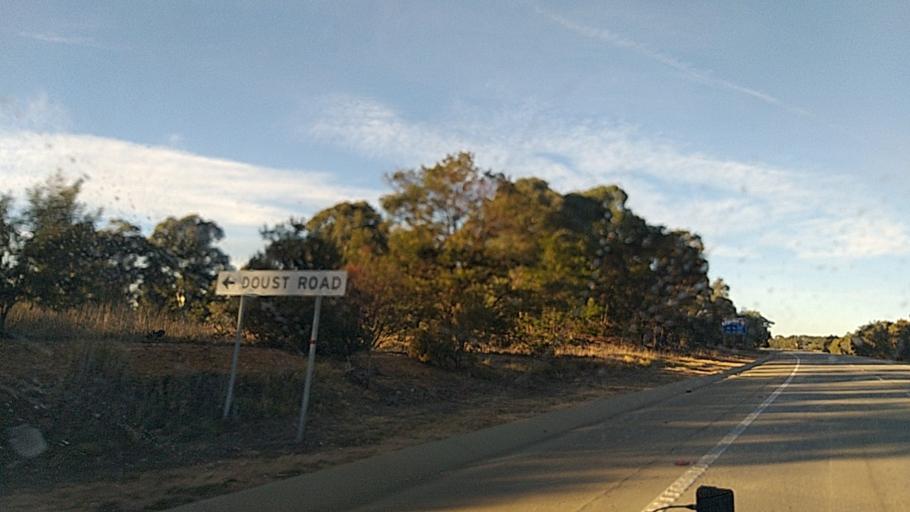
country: AU
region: New South Wales
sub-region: Yass Valley
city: Gundaroo
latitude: -35.1243
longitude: 149.3440
